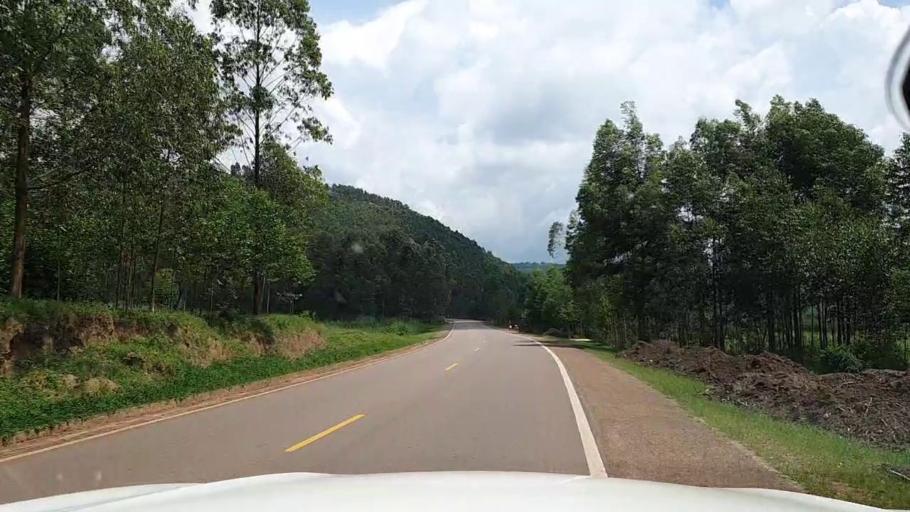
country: RW
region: Kigali
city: Kigali
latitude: -1.8235
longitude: 30.0819
